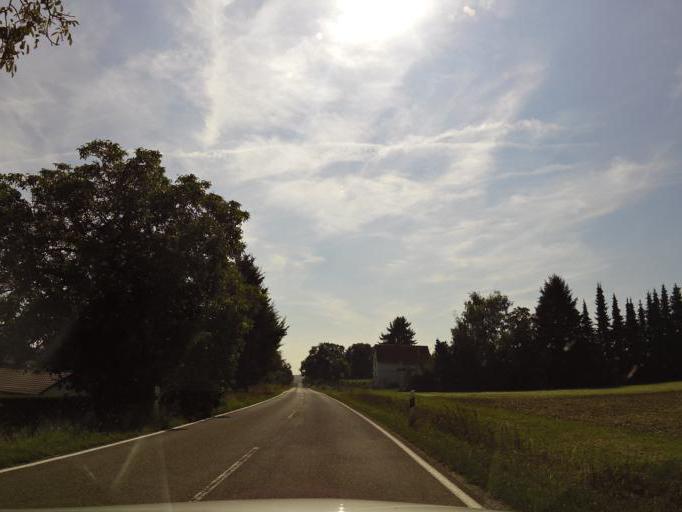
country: DE
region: Rheinland-Pfalz
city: Bechtolsheim
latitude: 49.8032
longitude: 8.1867
